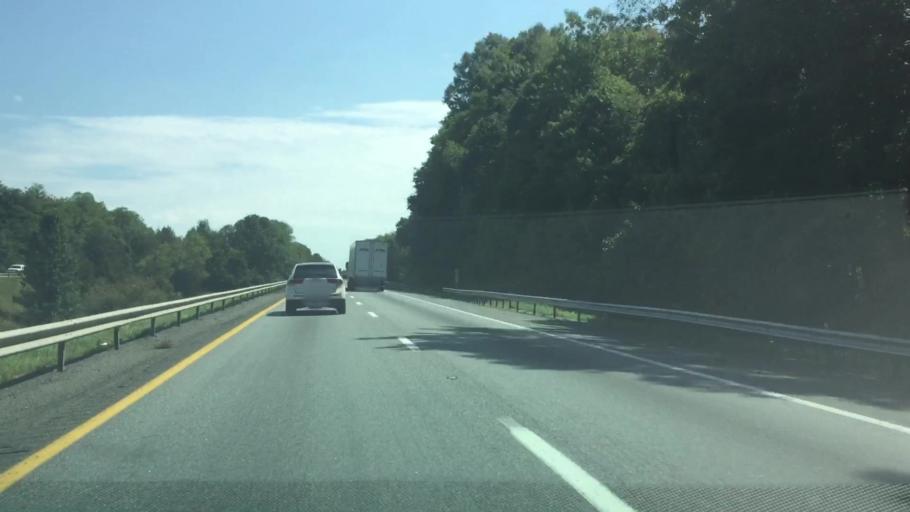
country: US
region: Virginia
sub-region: City of Radford
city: Radford
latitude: 37.0992
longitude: -80.5493
